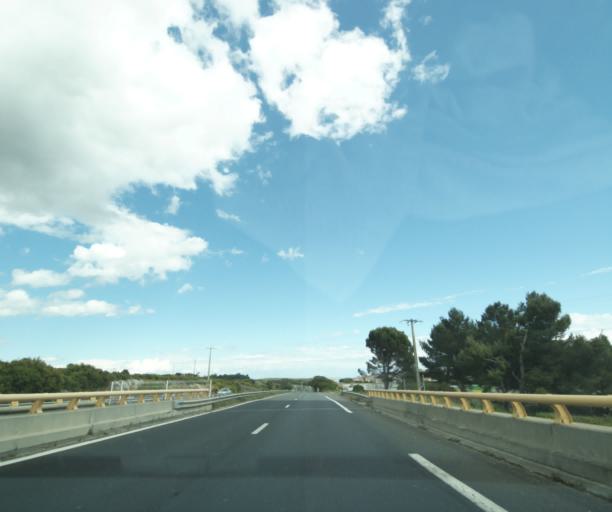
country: FR
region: Languedoc-Roussillon
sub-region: Departement de l'Herault
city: Murviel-les-Montpellier
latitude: 43.6309
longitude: 3.7651
